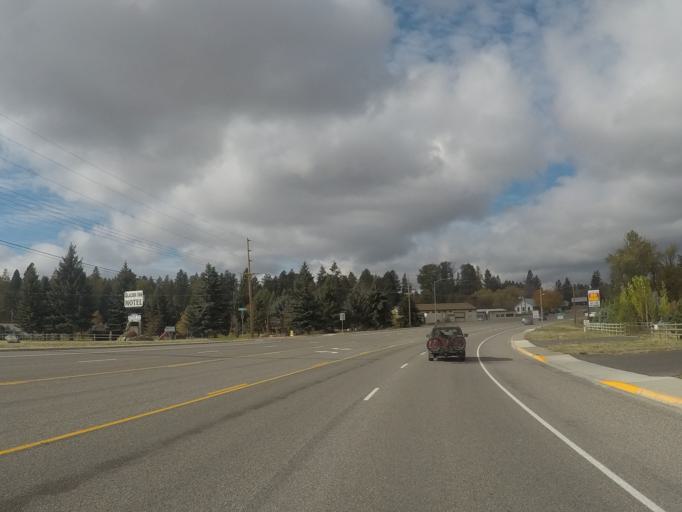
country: US
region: Montana
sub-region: Flathead County
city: Columbia Falls
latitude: 48.3672
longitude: -114.1758
